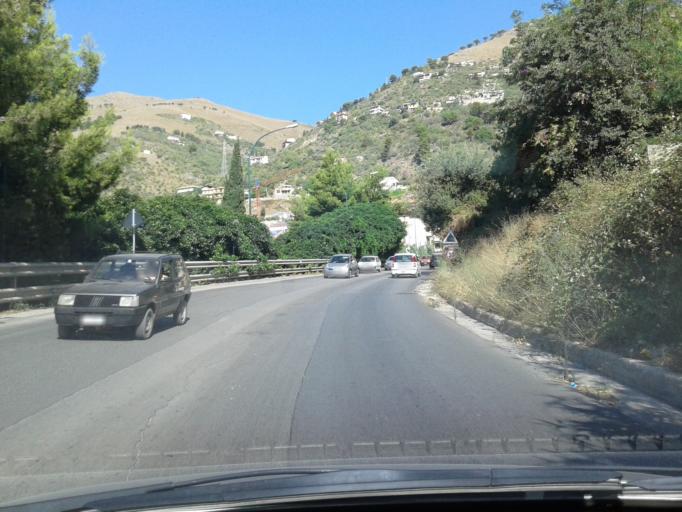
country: IT
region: Sicily
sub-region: Palermo
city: Monreale
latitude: 38.0746
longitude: 13.2833
